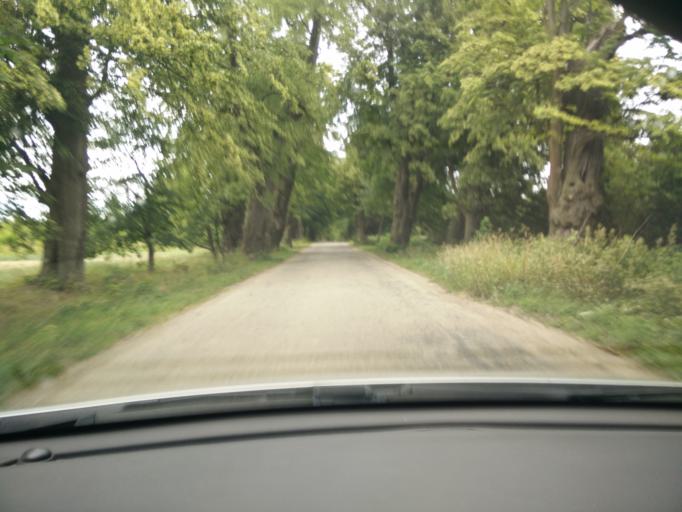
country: PL
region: Pomeranian Voivodeship
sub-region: Powiat pucki
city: Mrzezino
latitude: 54.6817
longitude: 18.4610
